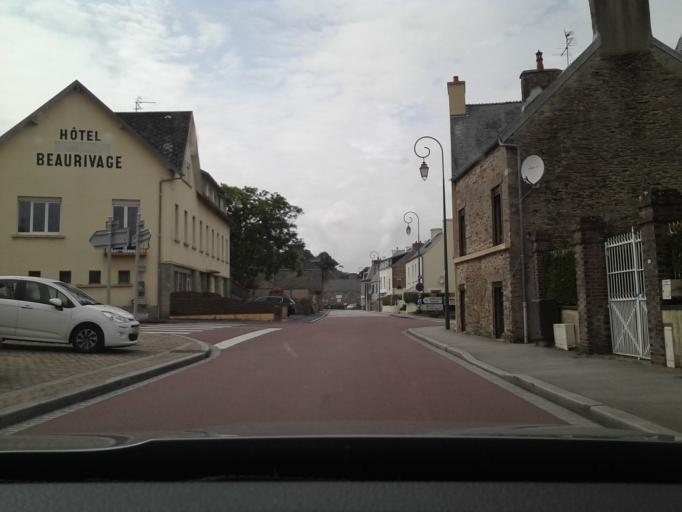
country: FR
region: Lower Normandy
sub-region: Departement de la Manche
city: Urville-Nacqueville
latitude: 49.6737
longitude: -1.7411
